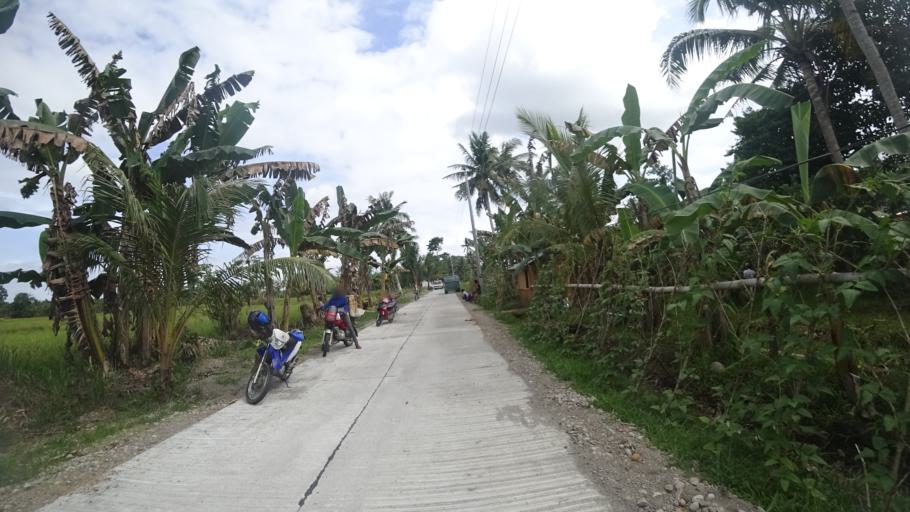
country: PH
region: Eastern Visayas
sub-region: Province of Leyte
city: Santa Fe
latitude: 11.1734
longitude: 124.8877
